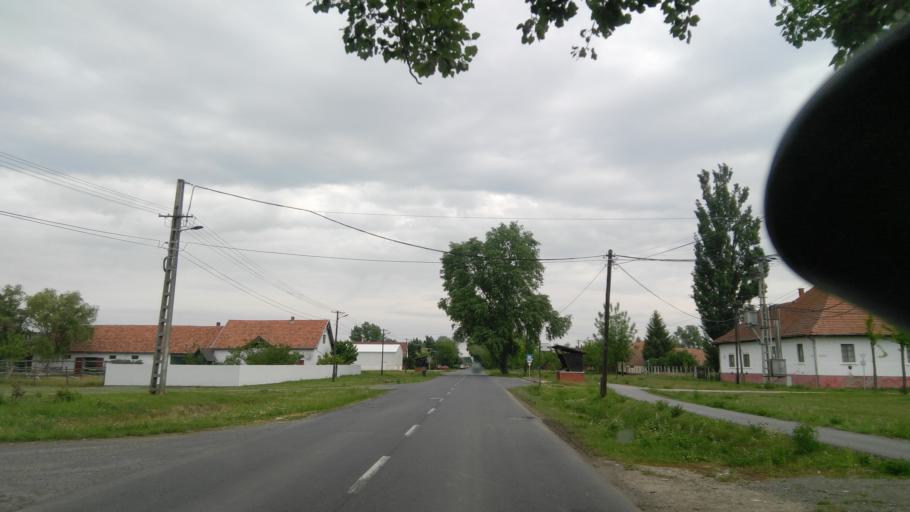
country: HU
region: Bekes
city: Veszto
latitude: 46.9030
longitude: 21.2539
